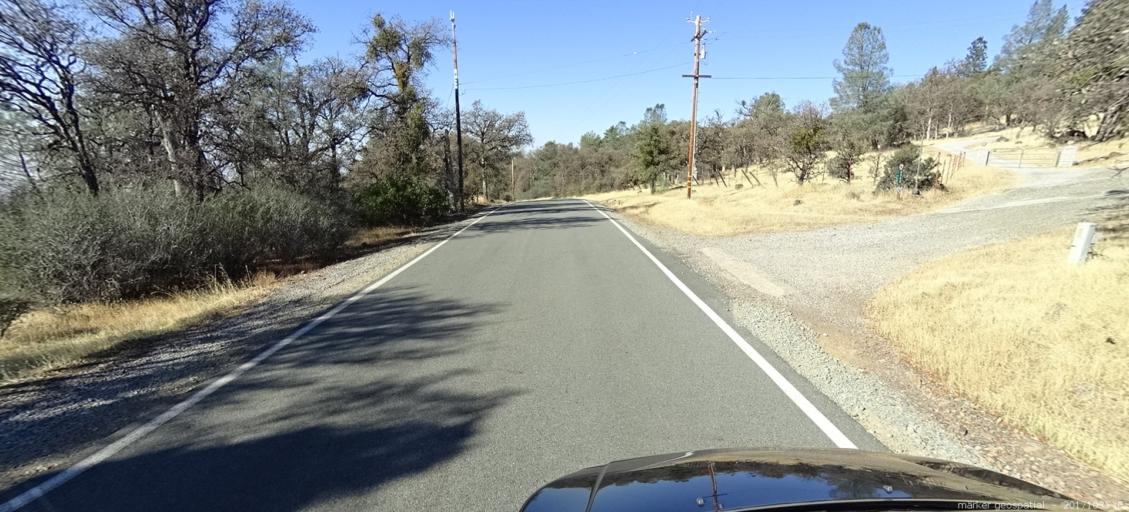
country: US
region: California
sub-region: Shasta County
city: Shingletown
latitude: 40.4711
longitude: -121.8830
